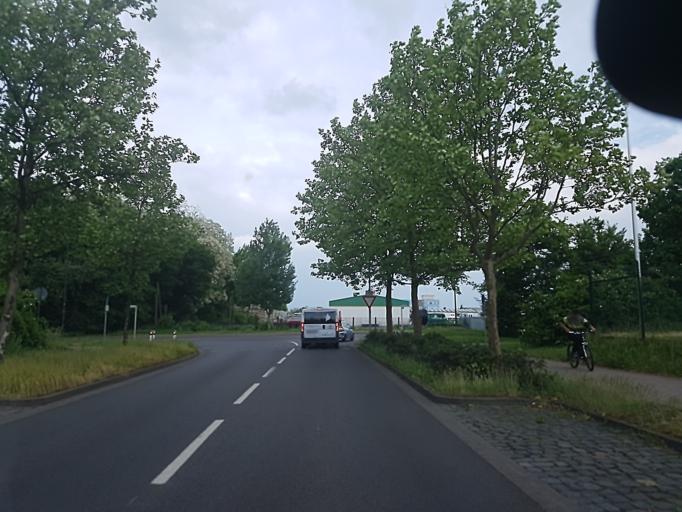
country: DE
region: Saxony-Anhalt
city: Nudersdorf
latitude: 51.8850
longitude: 12.5734
